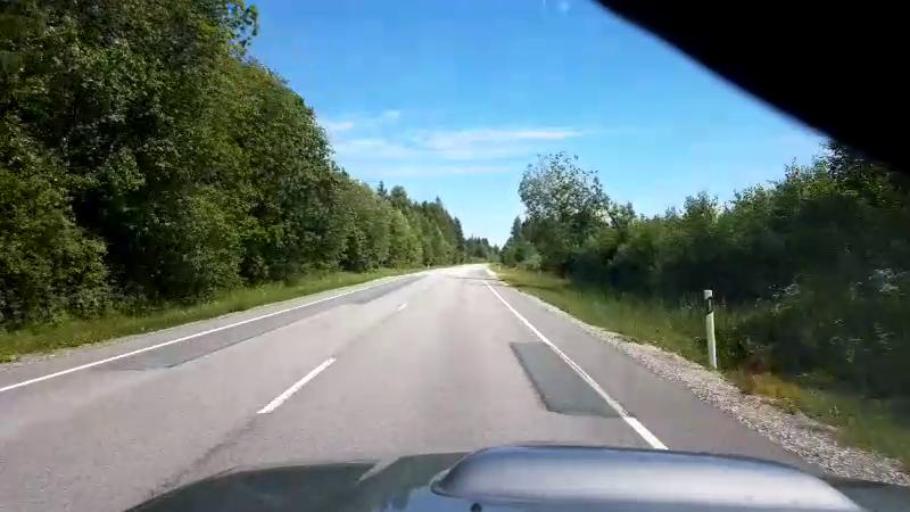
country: EE
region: Jaervamaa
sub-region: Koeru vald
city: Koeru
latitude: 58.9733
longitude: 26.1237
